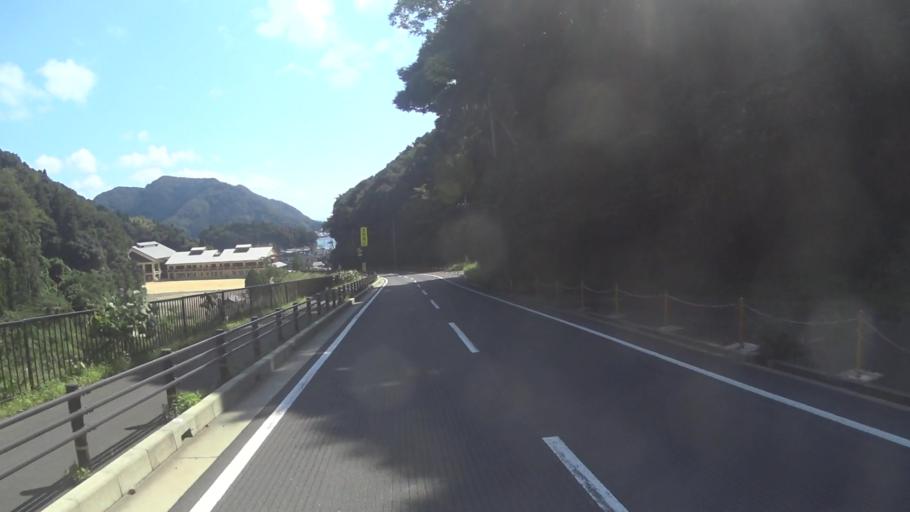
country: JP
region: Kyoto
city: Miyazu
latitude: 35.6804
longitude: 135.2857
